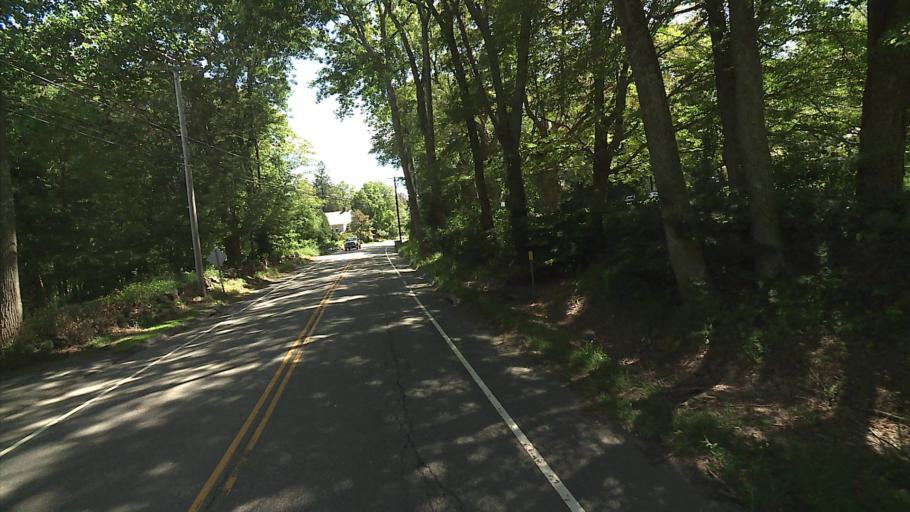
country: US
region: Connecticut
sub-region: Windham County
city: Windham
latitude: 41.7883
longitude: -72.0562
